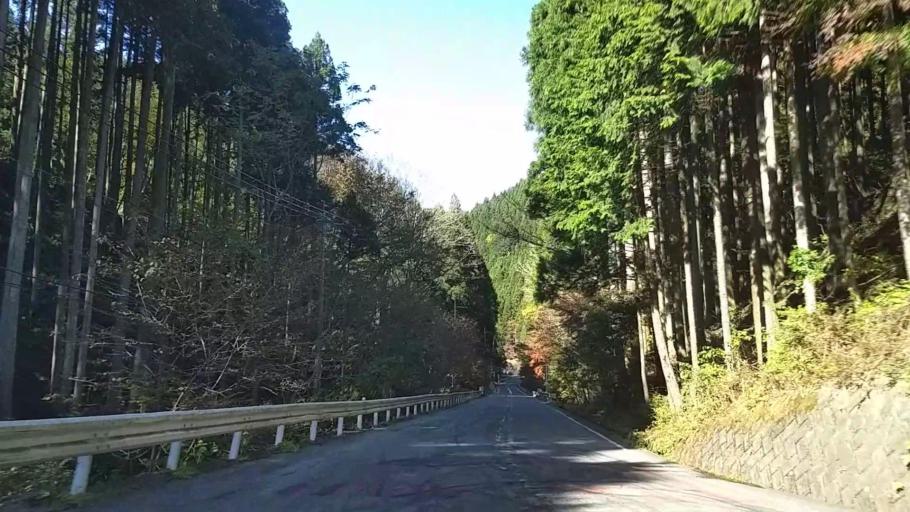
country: JP
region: Yamanashi
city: Otsuki
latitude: 35.7344
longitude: 138.9727
